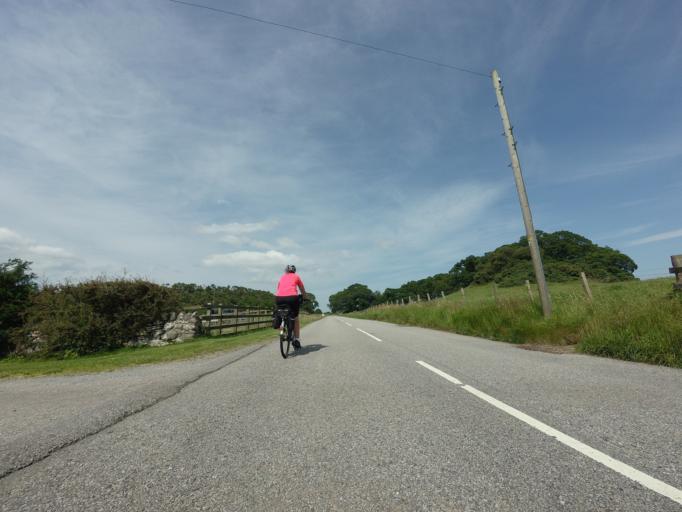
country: GB
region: Scotland
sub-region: Highland
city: Tain
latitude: 57.8496
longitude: -4.2033
